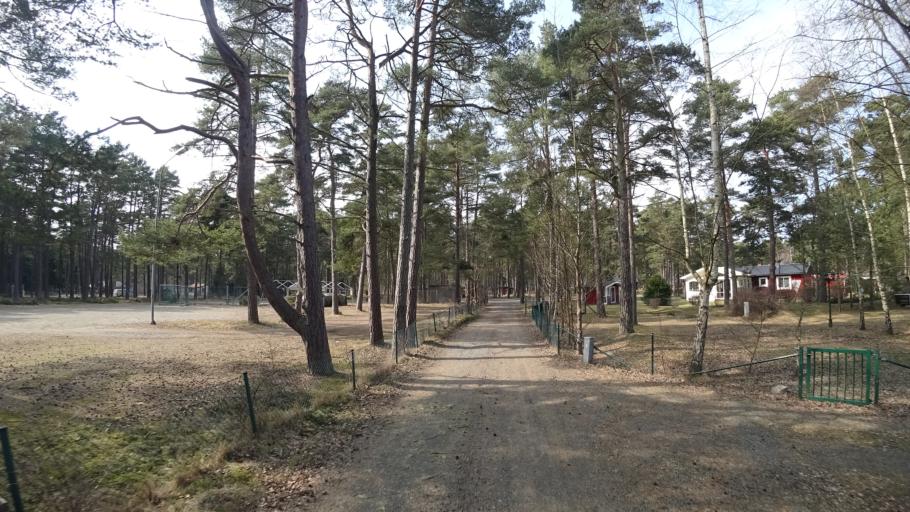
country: SE
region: Skane
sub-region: Kristianstads Kommun
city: Ahus
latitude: 55.9450
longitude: 14.3226
